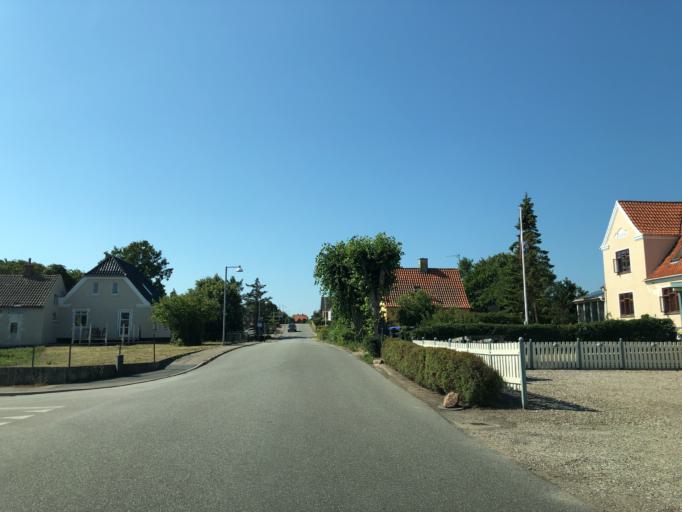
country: DK
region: Zealand
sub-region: Odsherred Kommune
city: Asnaes
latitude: 55.9709
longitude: 11.3660
